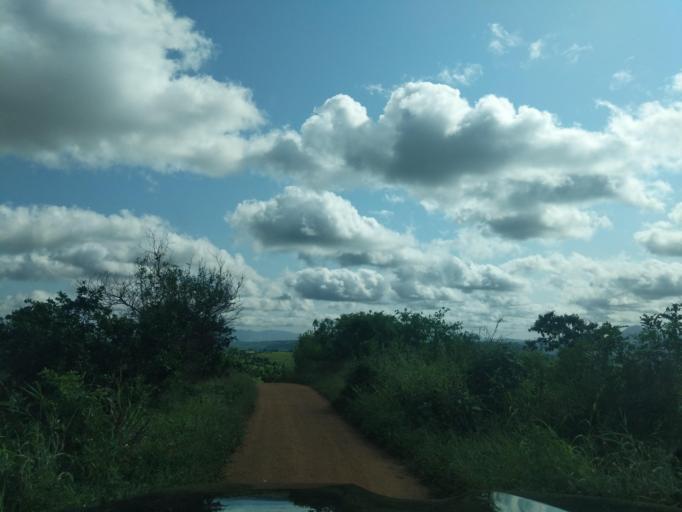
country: TZ
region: Tanga
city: Muheza
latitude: -5.4235
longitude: 38.6381
